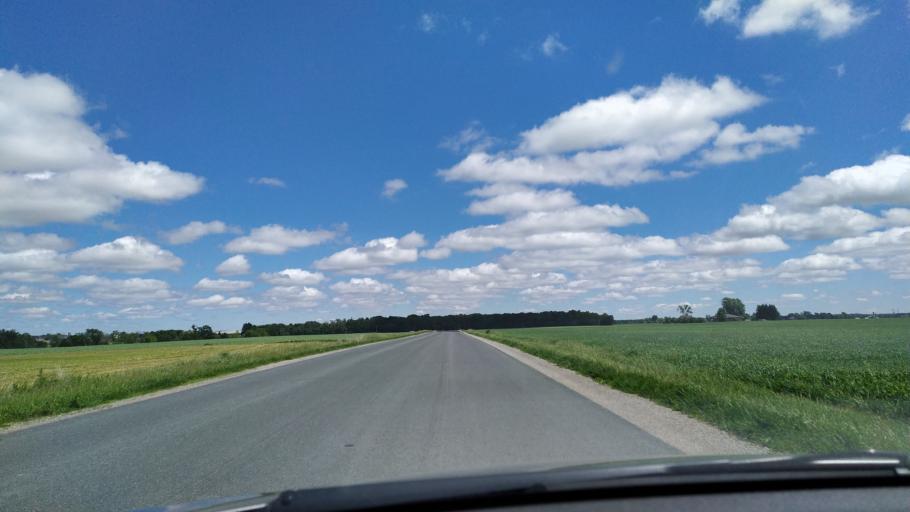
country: CA
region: Ontario
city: Huron East
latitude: 43.4540
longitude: -81.1902
